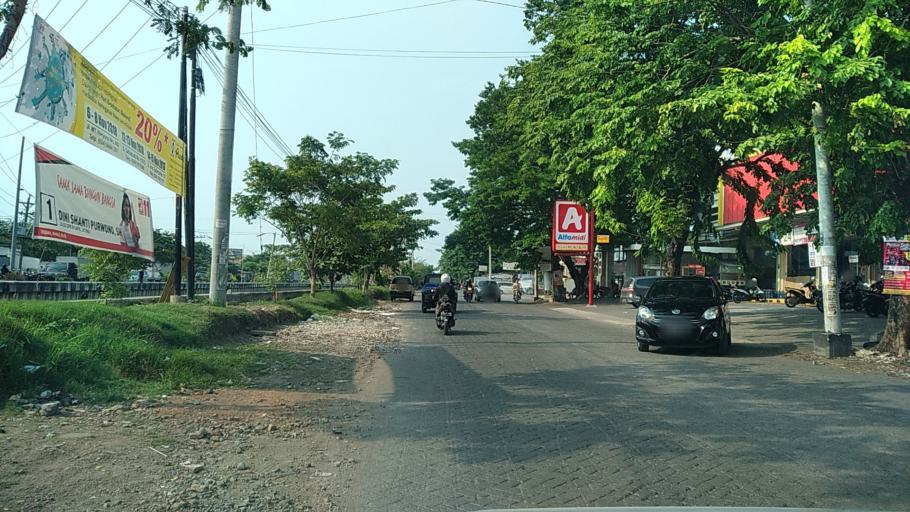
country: ID
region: Central Java
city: Semarang
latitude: -6.9654
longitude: 110.4112
